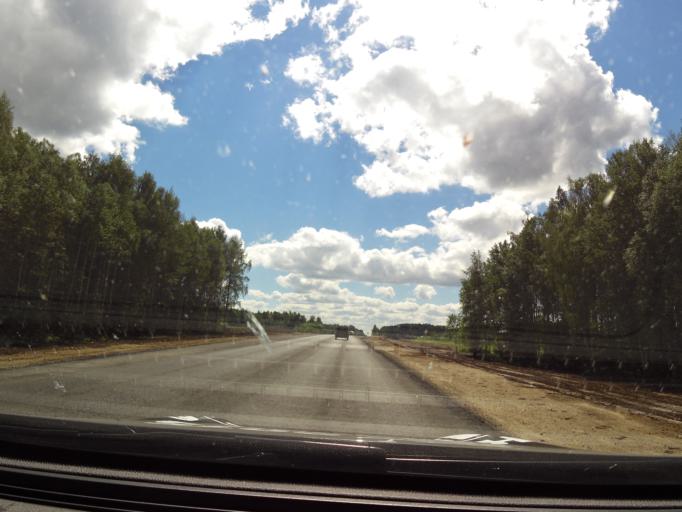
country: RU
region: Vologda
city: Molochnoye
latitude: 59.3464
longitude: 39.6784
